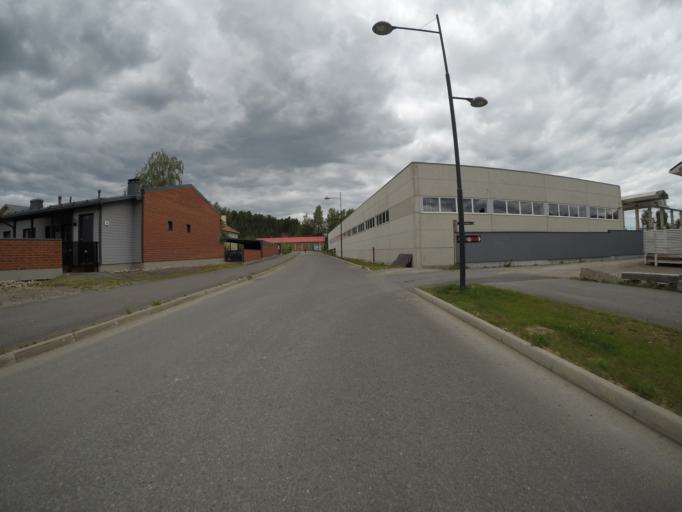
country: FI
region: Haeme
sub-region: Haemeenlinna
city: Haemeenlinna
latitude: 60.9923
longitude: 24.4358
